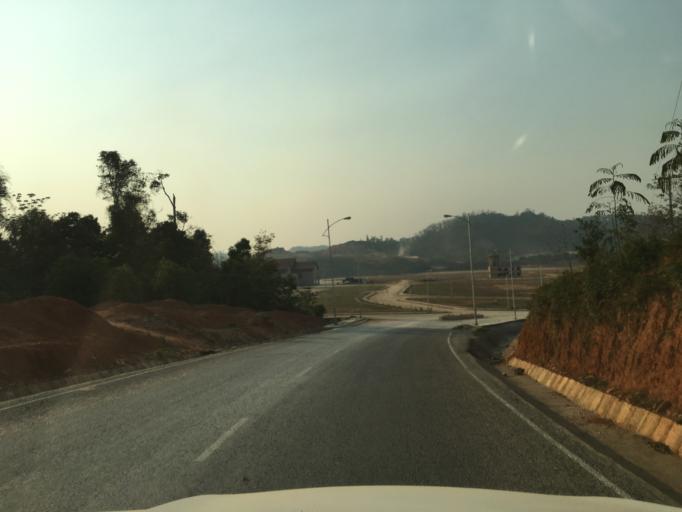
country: LA
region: Houaphan
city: Xam Nua
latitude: 20.6096
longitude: 104.0726
